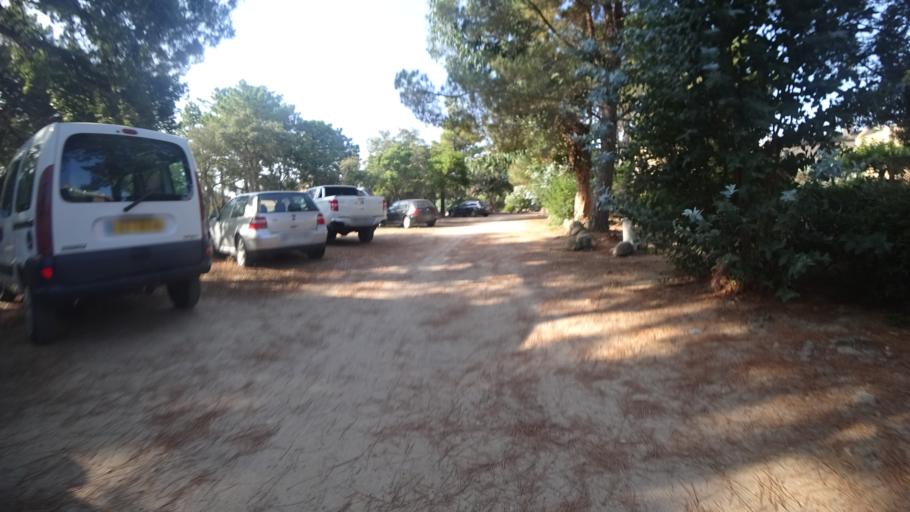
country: FR
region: Corsica
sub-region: Departement de la Corse-du-Sud
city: Porto-Vecchio
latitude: 41.6386
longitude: 9.3428
